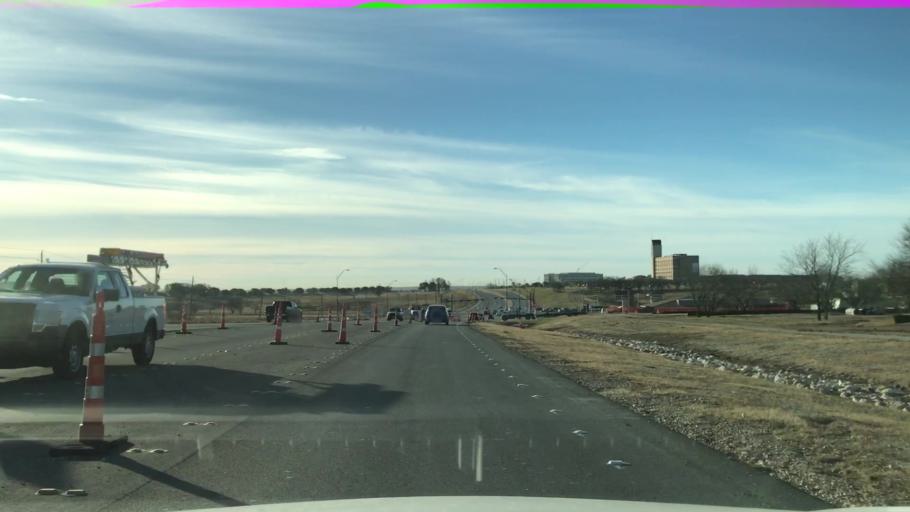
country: US
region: Texas
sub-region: Williamson County
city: Georgetown
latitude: 30.5762
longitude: -97.6516
